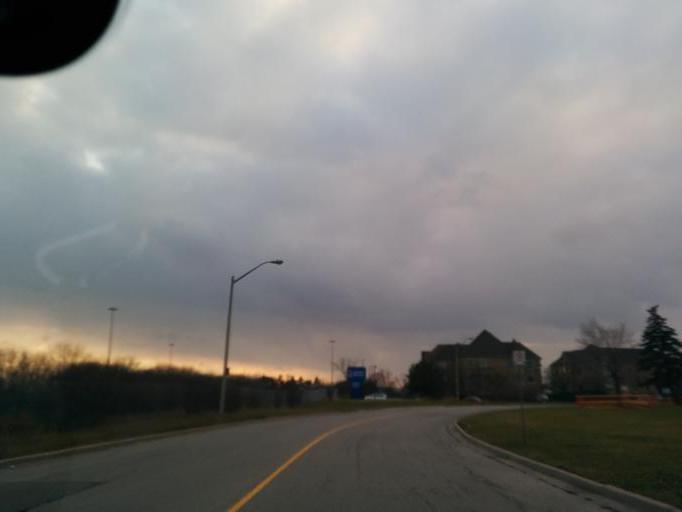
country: CA
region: Ontario
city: Oakville
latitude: 43.4649
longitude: -79.6807
